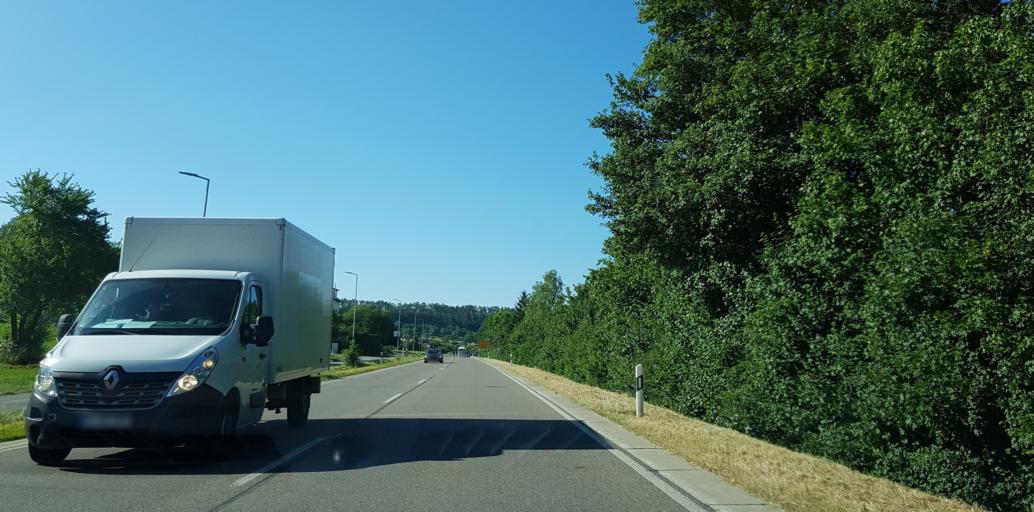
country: DE
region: Baden-Wuerttemberg
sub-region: Tuebingen Region
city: Allmendingen
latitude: 48.3289
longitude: 9.7292
